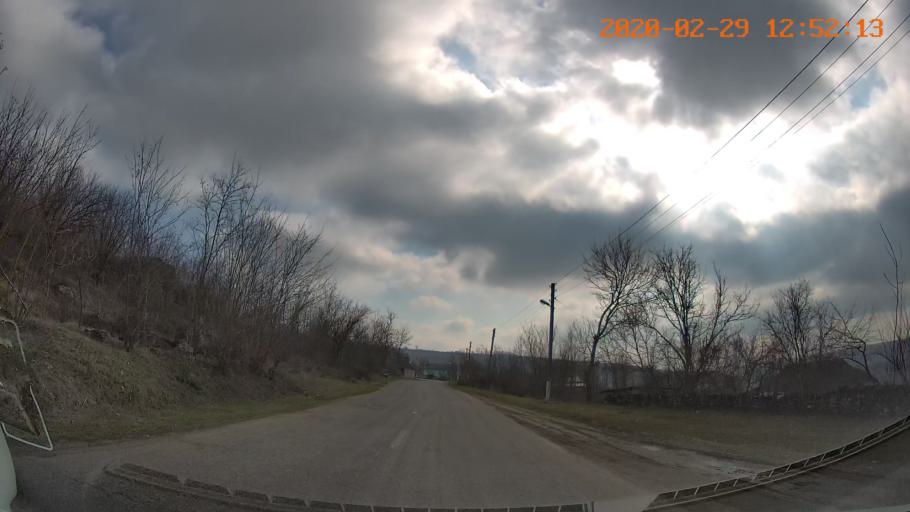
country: MD
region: Telenesti
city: Camenca
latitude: 48.1133
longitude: 28.7323
